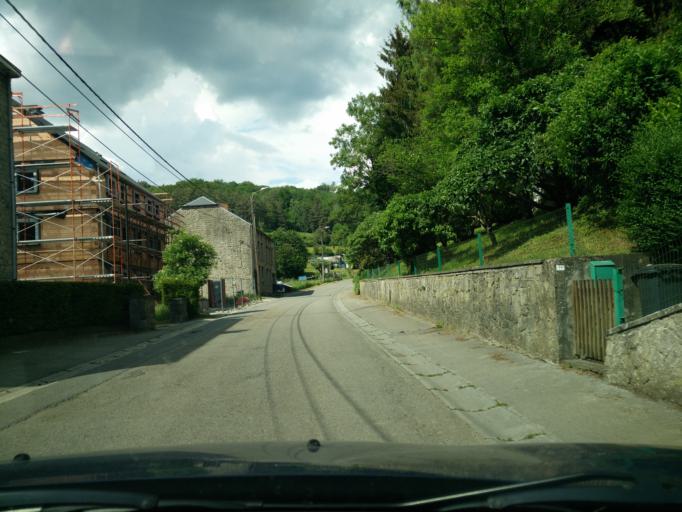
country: FR
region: Champagne-Ardenne
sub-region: Departement des Ardennes
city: Vireux-Molhain
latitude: 50.0823
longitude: 4.6335
